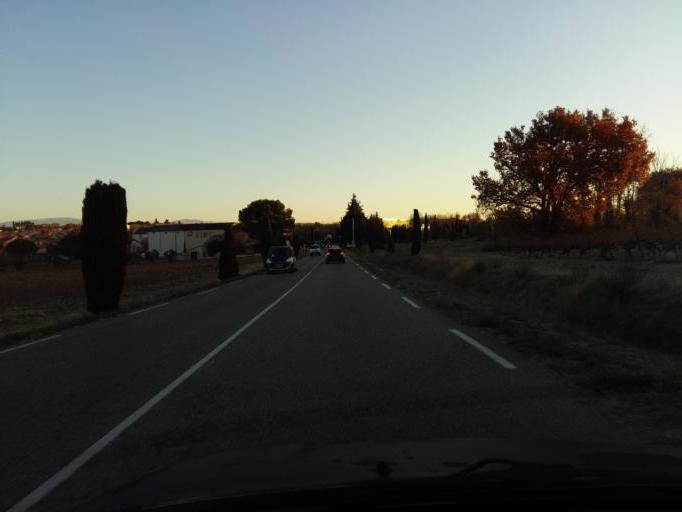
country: FR
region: Rhone-Alpes
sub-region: Departement de la Drome
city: Tulette
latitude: 44.2815
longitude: 4.9265
